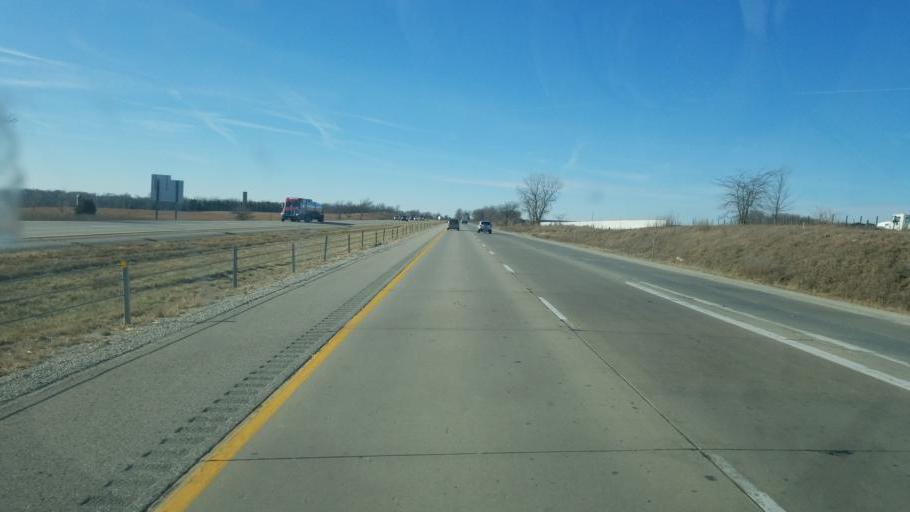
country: US
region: Iowa
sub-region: Dallas County
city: De Soto
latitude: 41.5398
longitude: -94.0179
